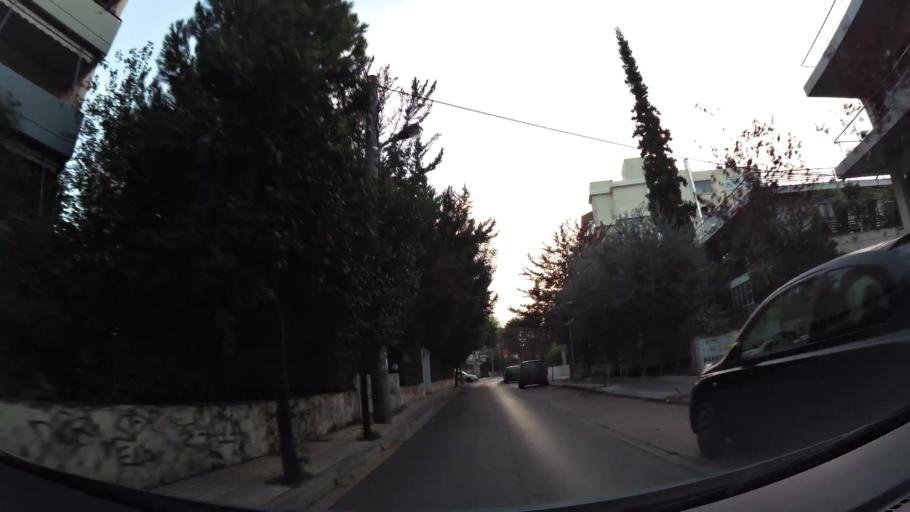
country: GR
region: Attica
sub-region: Nomarchia Athinas
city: Agia Paraskevi
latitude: 38.0168
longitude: 23.8320
